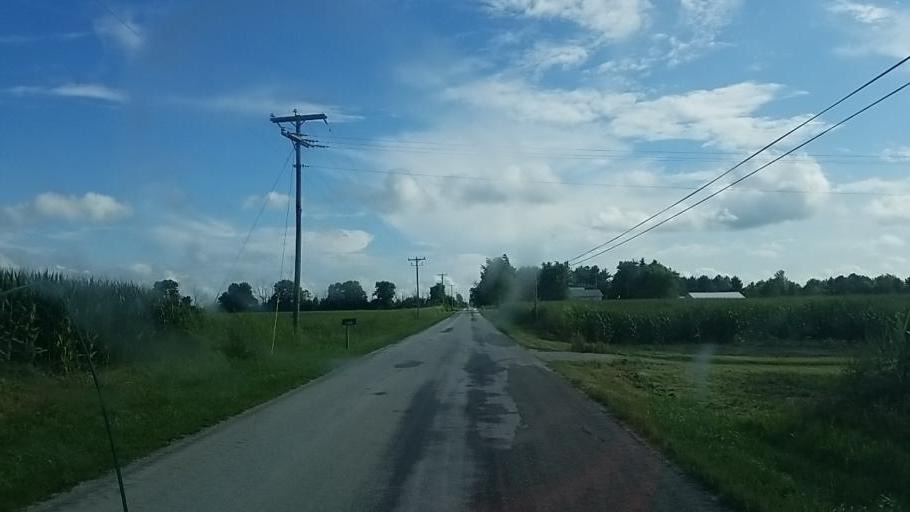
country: US
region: Ohio
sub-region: Hardin County
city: Kenton
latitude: 40.6783
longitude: -83.5380
